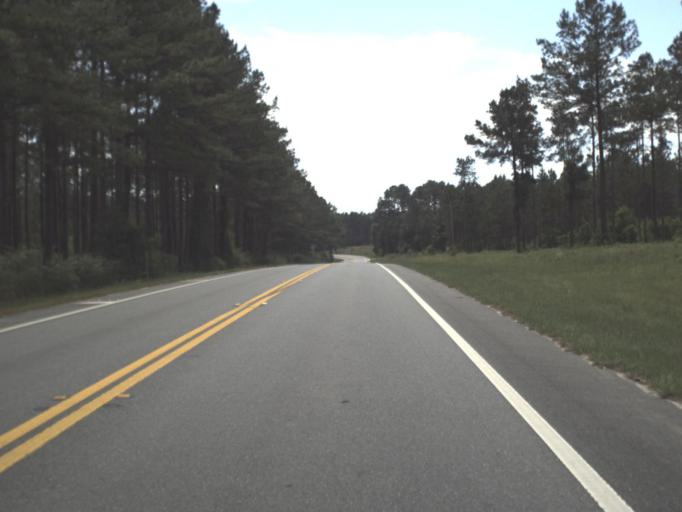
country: US
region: Florida
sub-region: Gulf County
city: Wewahitchka
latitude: 30.2432
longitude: -85.2078
